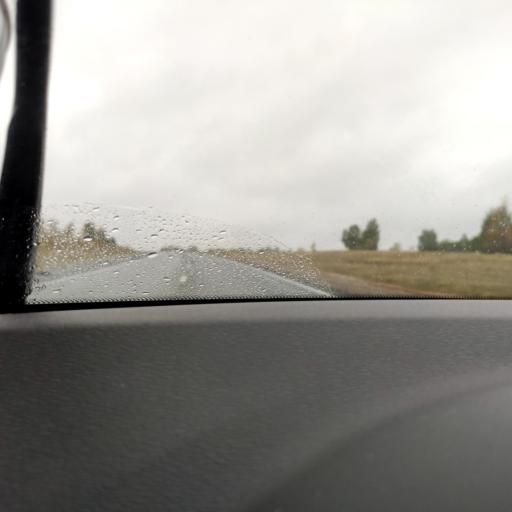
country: RU
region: Samara
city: Mirnyy
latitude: 53.6348
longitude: 50.2395
